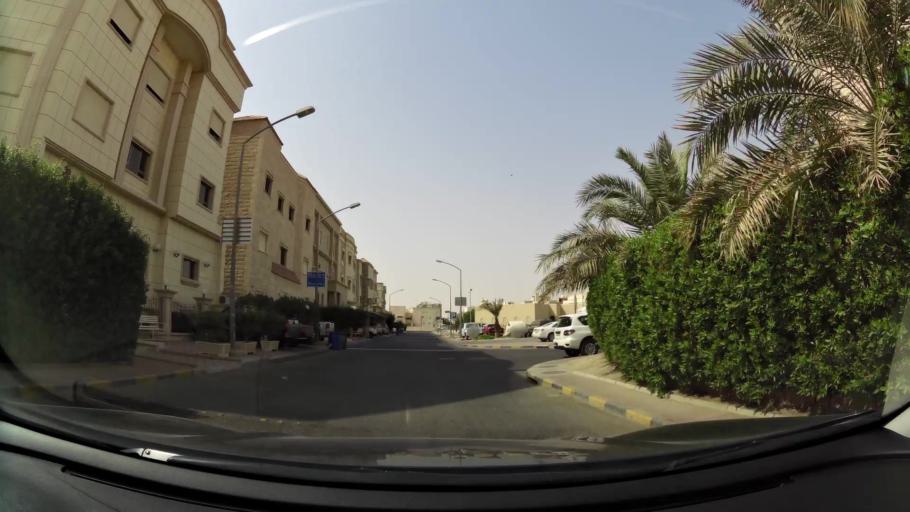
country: KW
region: Muhafazat al Jahra'
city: Al Jahra'
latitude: 29.3042
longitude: 47.6959
